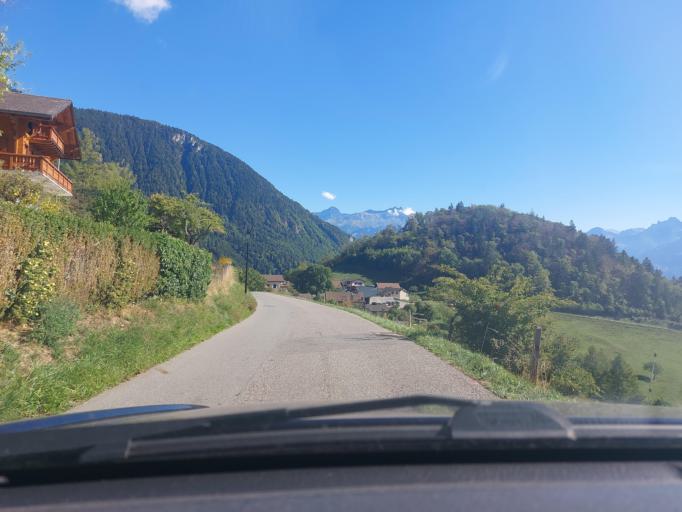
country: CH
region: Vaud
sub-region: Aigle District
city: Aigle
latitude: 46.3503
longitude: 6.9578
